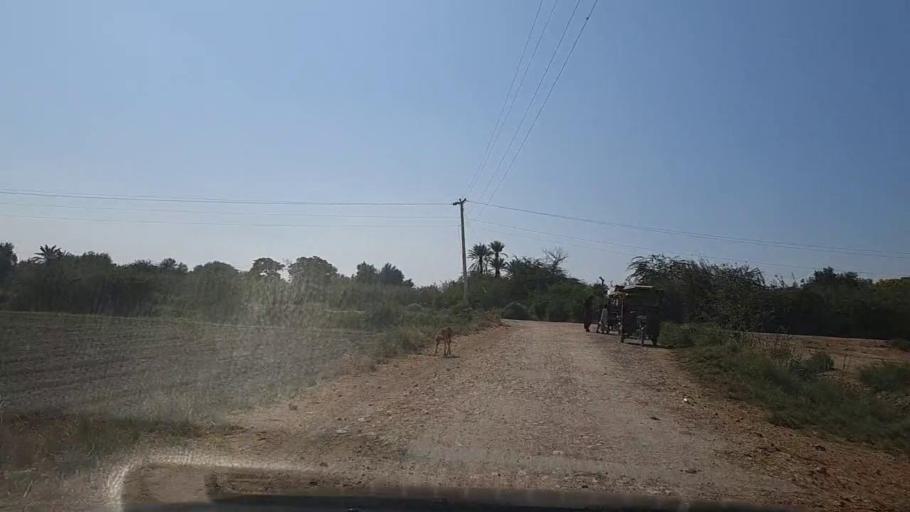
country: PK
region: Sindh
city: Mirpur Sakro
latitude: 24.5937
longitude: 67.7786
